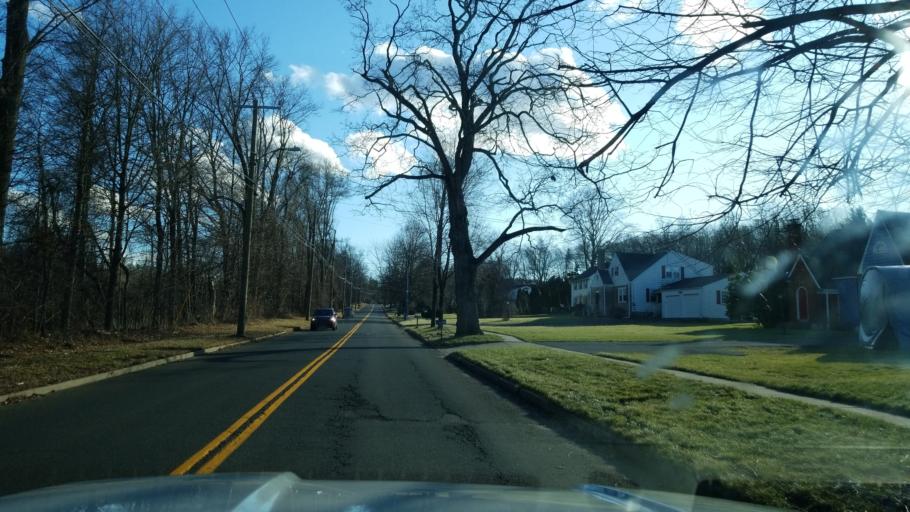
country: US
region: Connecticut
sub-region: Middlesex County
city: Middletown
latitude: 41.5472
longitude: -72.6713
